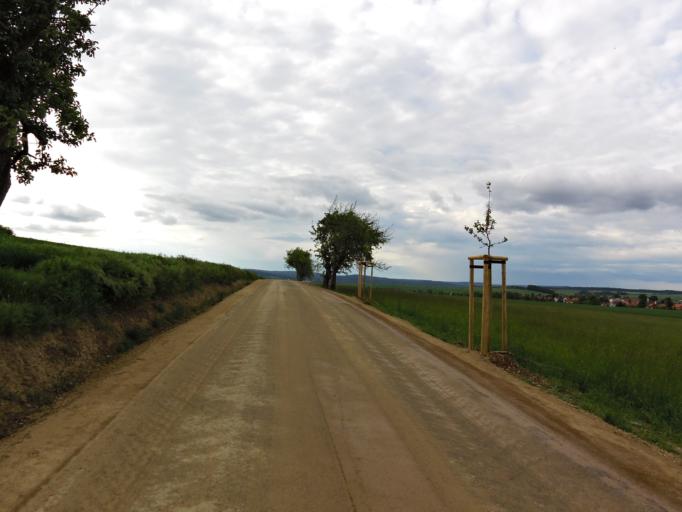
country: DE
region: Thuringia
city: Dippach
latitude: 50.9132
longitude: 10.0910
